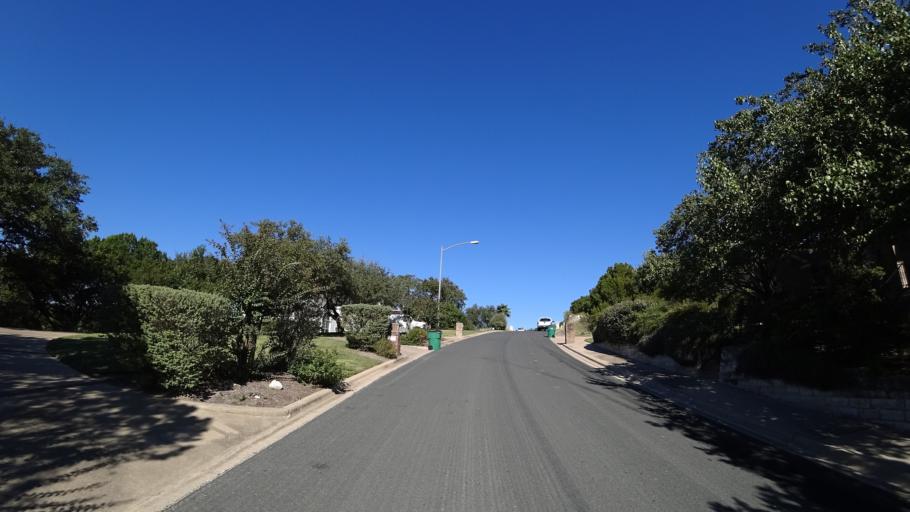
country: US
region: Texas
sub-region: Travis County
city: West Lake Hills
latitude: 30.3301
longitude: -97.7953
